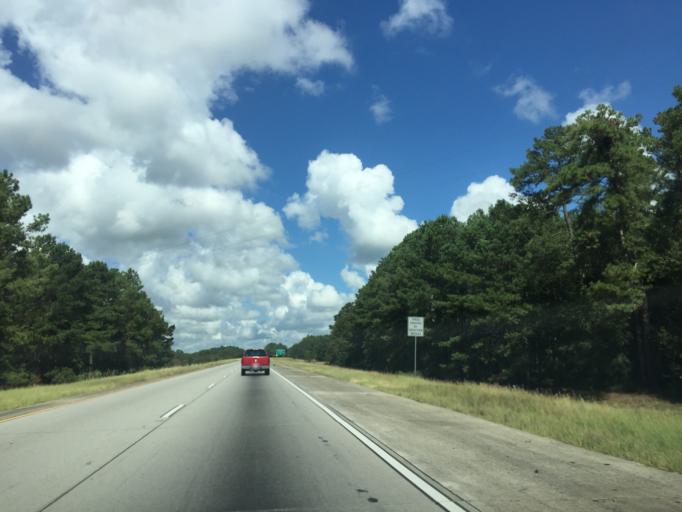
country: US
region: Georgia
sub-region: Candler County
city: Metter
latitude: 32.3344
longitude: -81.9441
